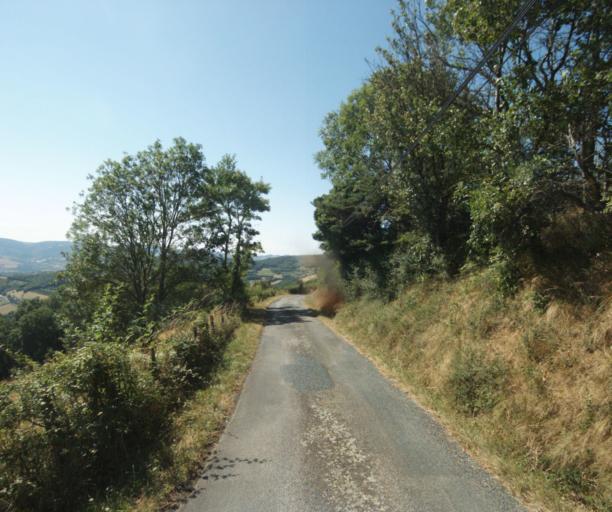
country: FR
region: Rhone-Alpes
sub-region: Departement du Rhone
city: Montrottier
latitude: 45.8027
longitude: 4.5065
